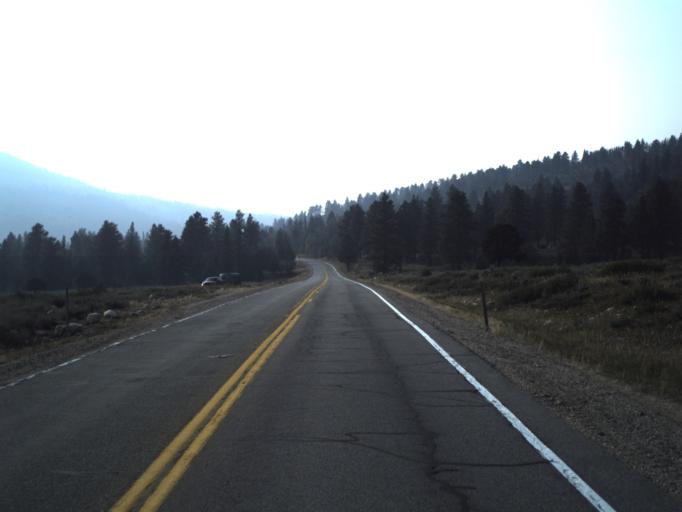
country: US
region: Utah
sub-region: Summit County
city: Francis
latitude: 40.5983
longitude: -111.0997
